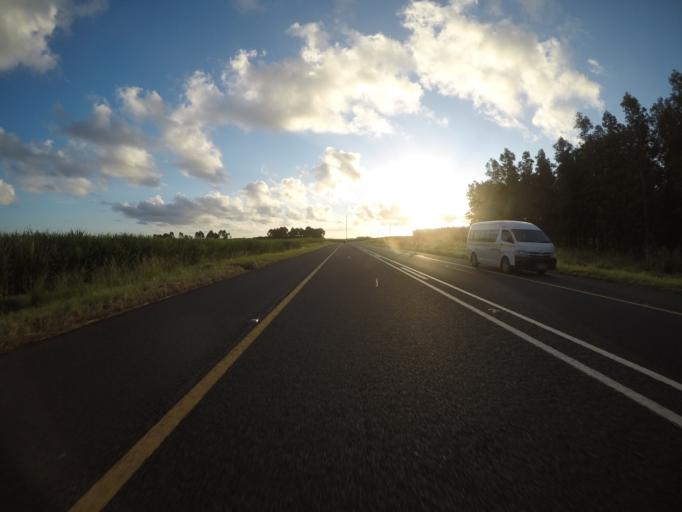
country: ZA
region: KwaZulu-Natal
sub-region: uThungulu District Municipality
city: Empangeni
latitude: -28.7005
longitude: 31.9716
